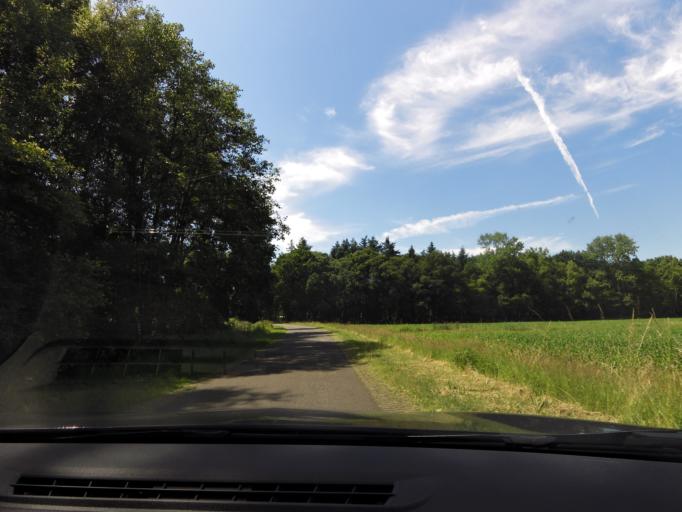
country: NL
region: Overijssel
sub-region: Gemeente Wierden
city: Wierden
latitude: 52.3242
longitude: 6.5480
